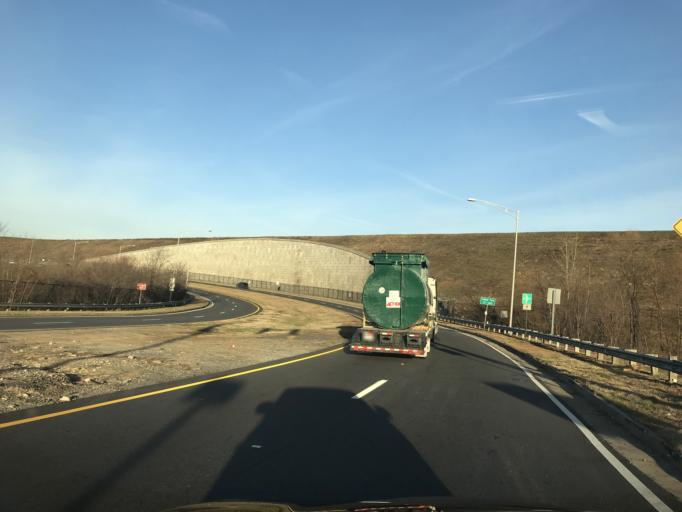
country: US
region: Georgia
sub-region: Fulton County
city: College Park
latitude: 33.6186
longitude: -84.4387
